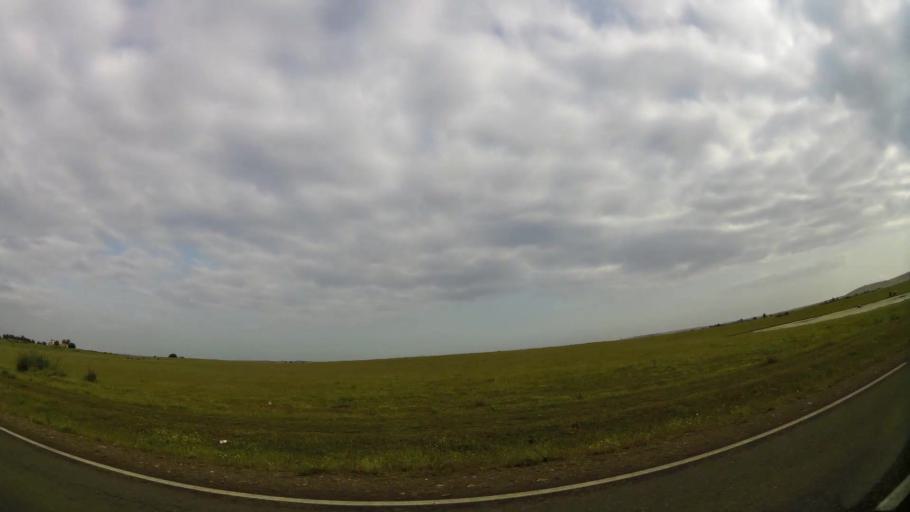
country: MA
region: Rabat-Sale-Zemmour-Zaer
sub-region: Khemisset
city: Khemisset
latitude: 33.7579
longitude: -6.1831
